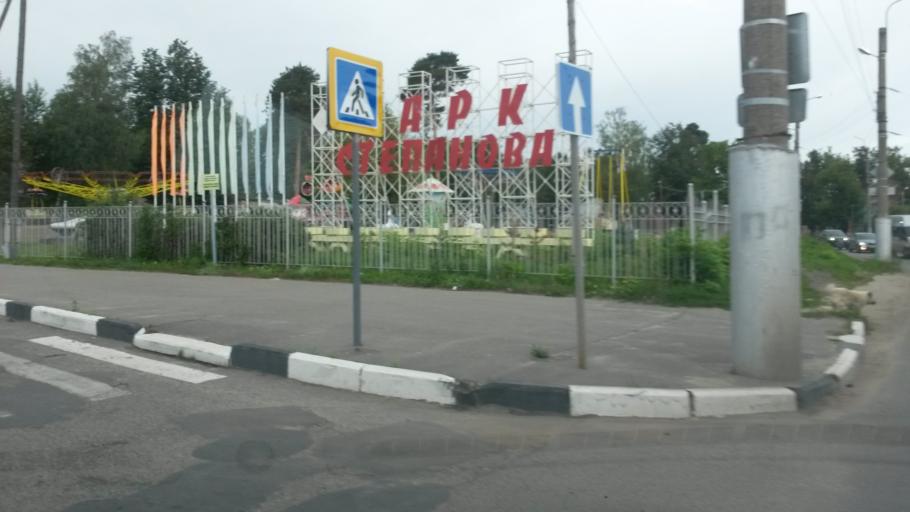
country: RU
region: Ivanovo
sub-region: Gorod Ivanovo
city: Ivanovo
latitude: 57.0213
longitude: 40.9503
